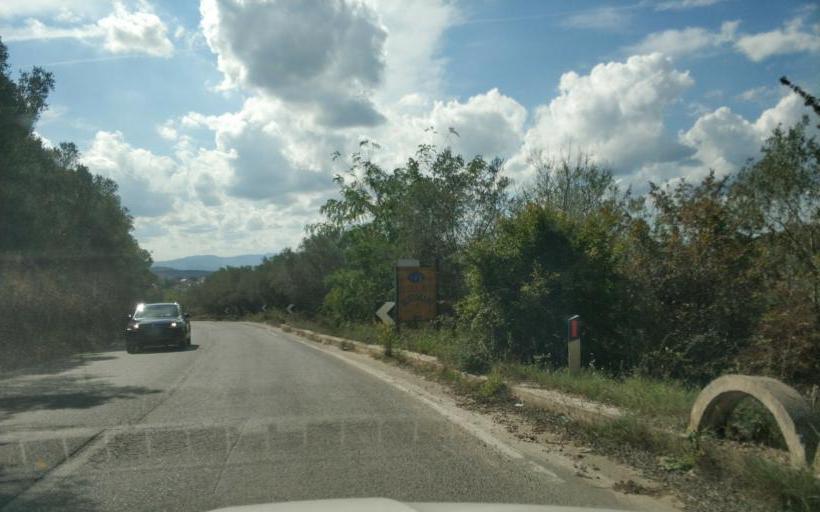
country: AL
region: Durres
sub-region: Rrethi i Krujes
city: Kruje
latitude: 41.4849
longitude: 19.7663
